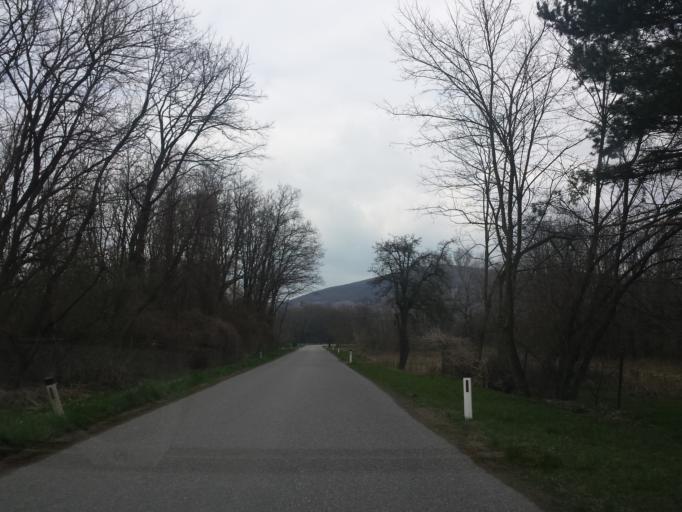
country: AT
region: Lower Austria
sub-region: Politischer Bezirk Bruck an der Leitha
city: Hainburg an der Donau
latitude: 48.1642
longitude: 16.9749
